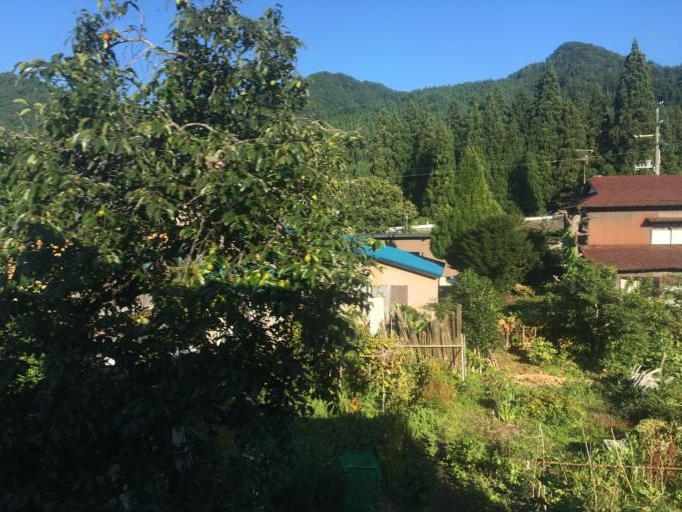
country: JP
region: Akita
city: Takanosu
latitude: 39.9945
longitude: 140.4011
